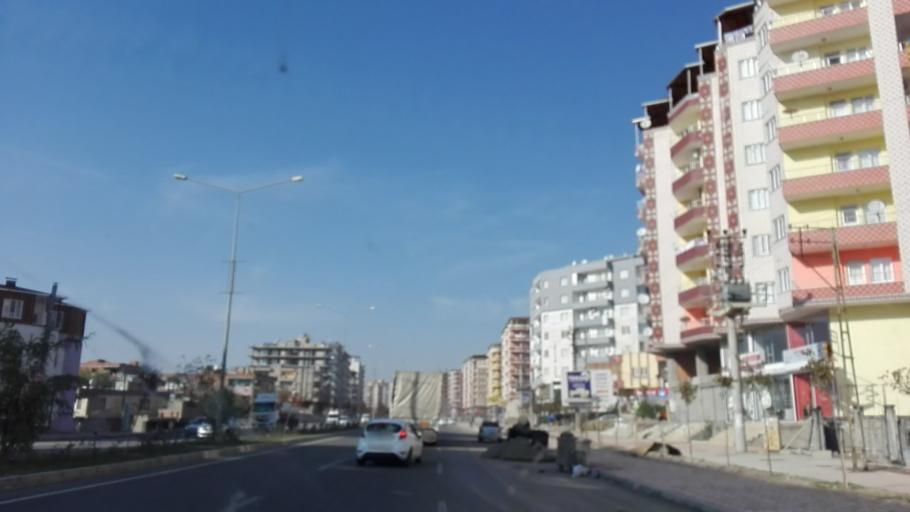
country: TR
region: Batman
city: Aydinkonak
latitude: 37.8961
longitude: 41.1484
